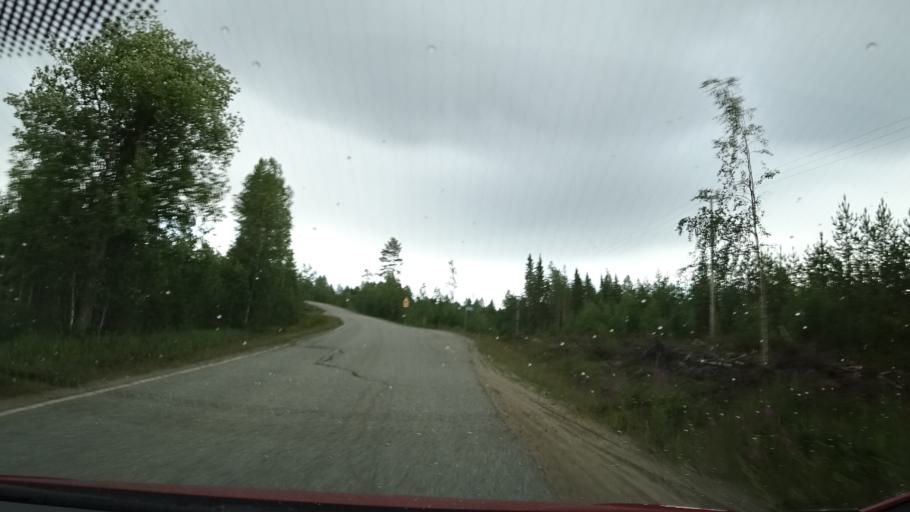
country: FI
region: Kainuu
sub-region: Kehys-Kainuu
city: Kuhmo
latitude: 63.9520
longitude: 29.2320
